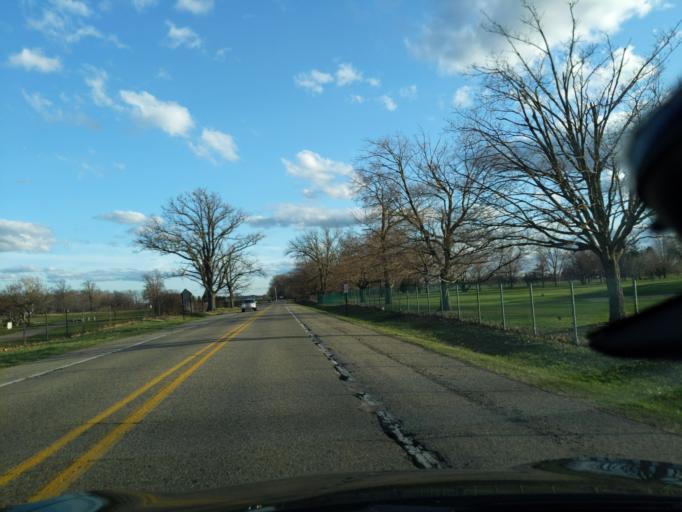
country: US
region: Michigan
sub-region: Ingham County
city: East Lansing
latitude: 42.7074
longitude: -84.4939
